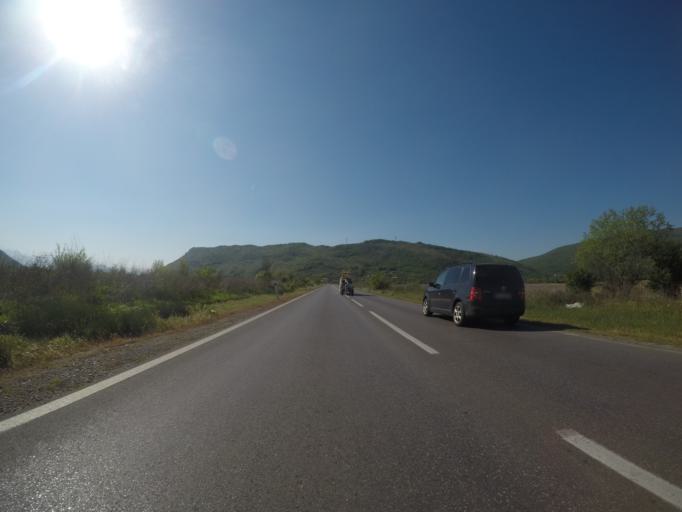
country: ME
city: Spuz
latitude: 42.4669
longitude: 19.1748
